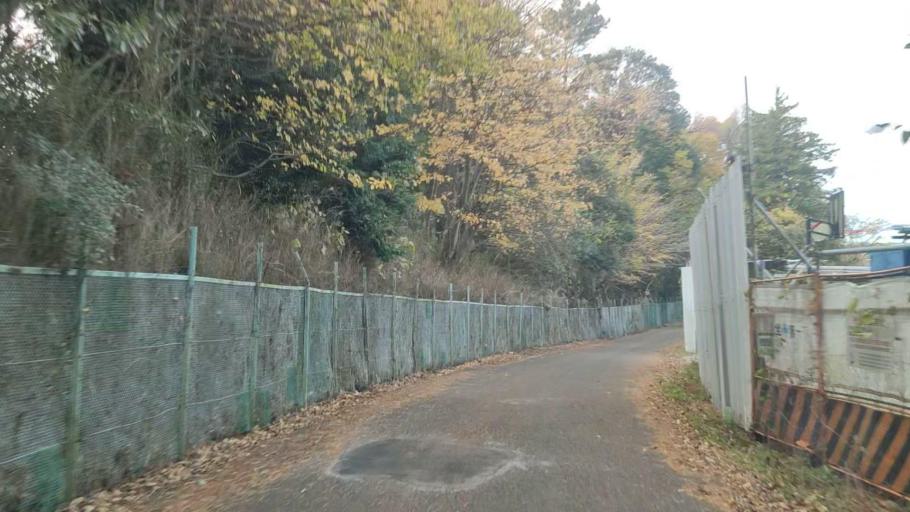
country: JP
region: Kanagawa
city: Minami-rinkan
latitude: 35.4906
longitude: 139.4939
